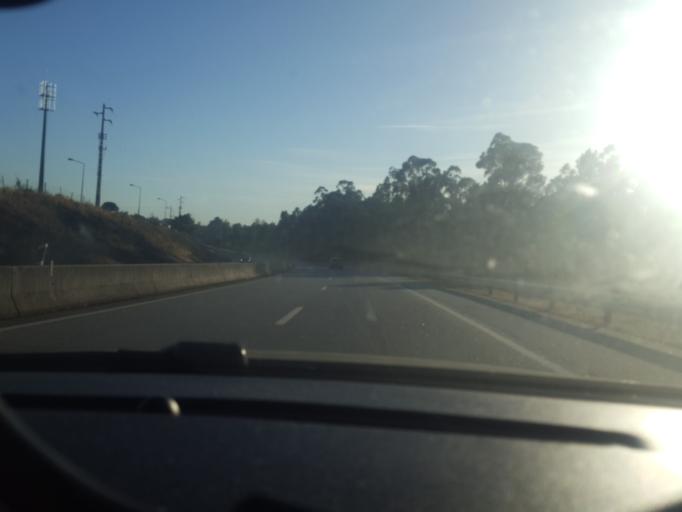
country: PT
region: Viseu
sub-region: Concelho de Carregal do Sal
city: Carregal do Sal
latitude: 40.4610
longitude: -7.9649
